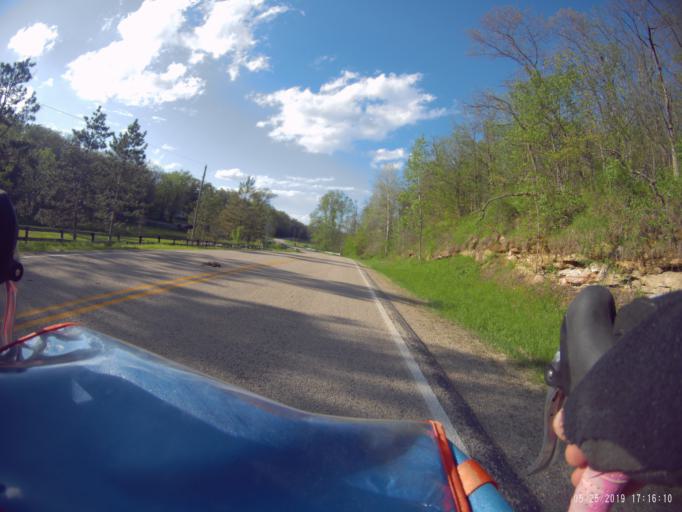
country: US
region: Wisconsin
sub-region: Dane County
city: Mount Horeb
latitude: 42.9688
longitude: -89.7896
